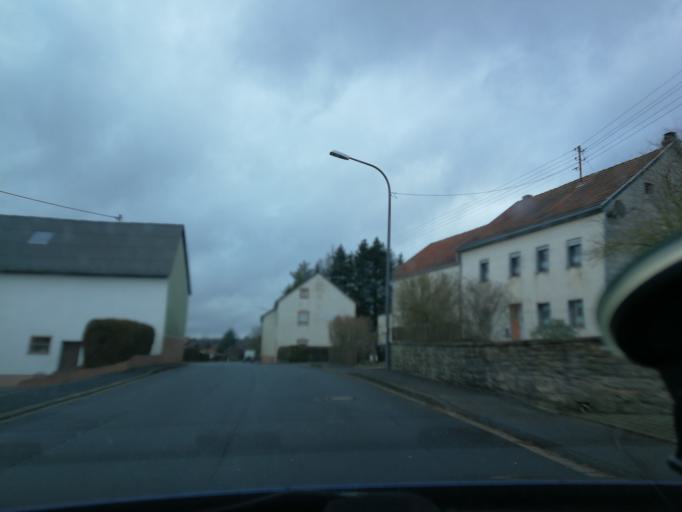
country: DE
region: Rheinland-Pfalz
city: Oberehe-Stroheich
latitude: 50.2860
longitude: 6.7547
